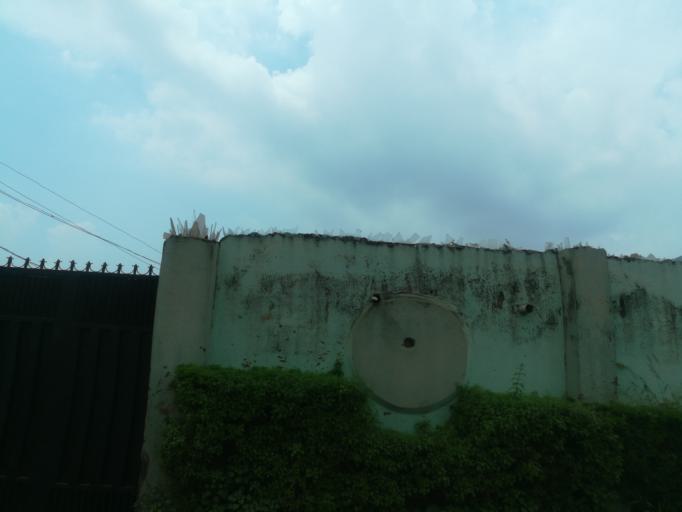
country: NG
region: Oyo
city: Ibadan
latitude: 7.4286
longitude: 3.9260
